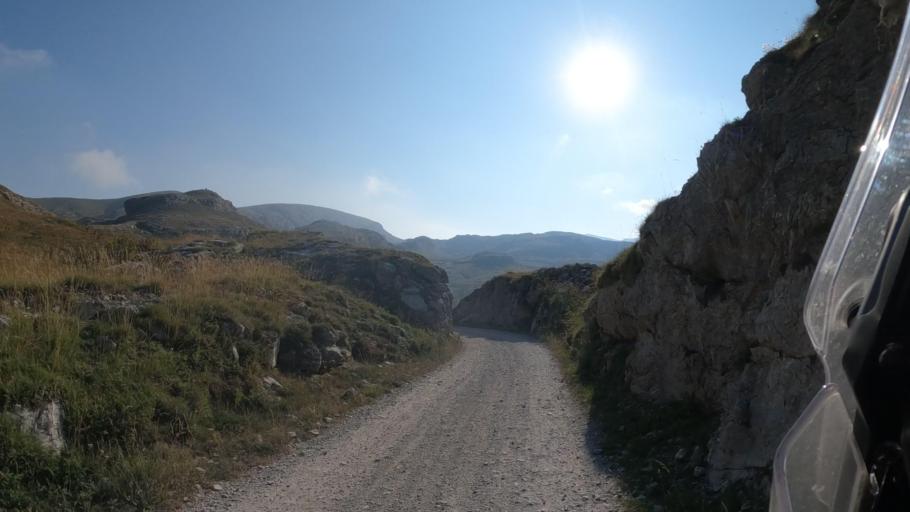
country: IT
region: Piedmont
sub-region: Provincia di Cuneo
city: Limone Piemonte
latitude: 44.1704
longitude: 7.6399
